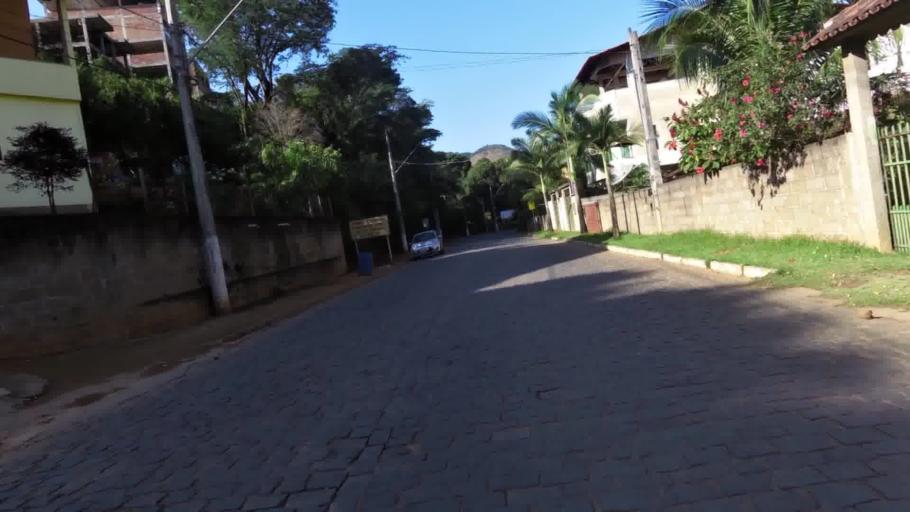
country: BR
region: Espirito Santo
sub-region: Alfredo Chaves
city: Alfredo Chaves
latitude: -20.6320
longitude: -40.7596
